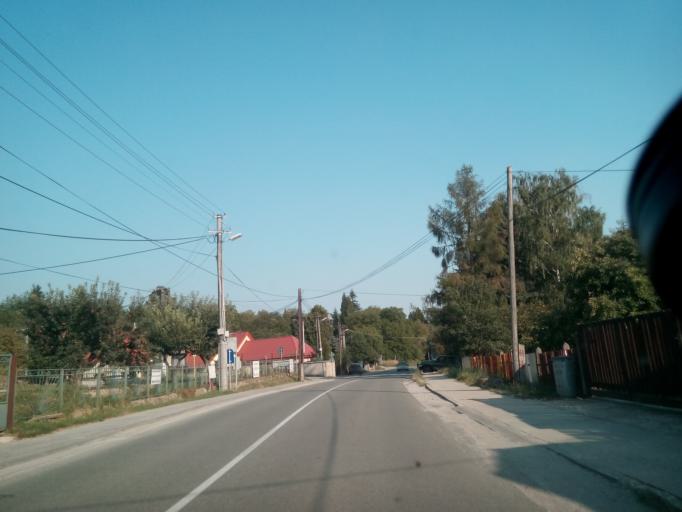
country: SK
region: Kosicky
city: Kosice
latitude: 48.7145
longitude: 21.1956
